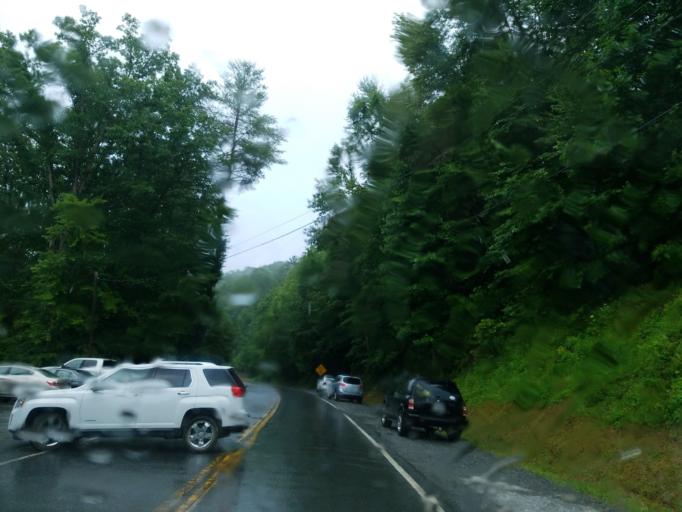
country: US
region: Georgia
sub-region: Fannin County
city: Blue Ridge
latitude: 34.7829
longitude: -84.2645
